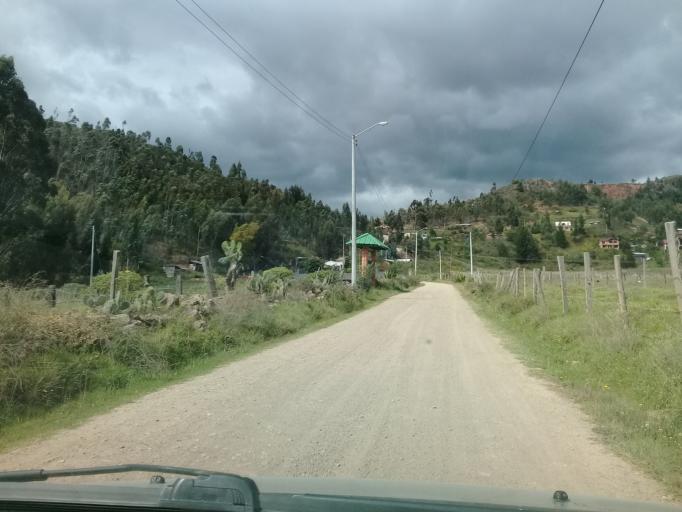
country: CO
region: Cundinamarca
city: Cucunuba
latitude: 5.2548
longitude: -73.7663
